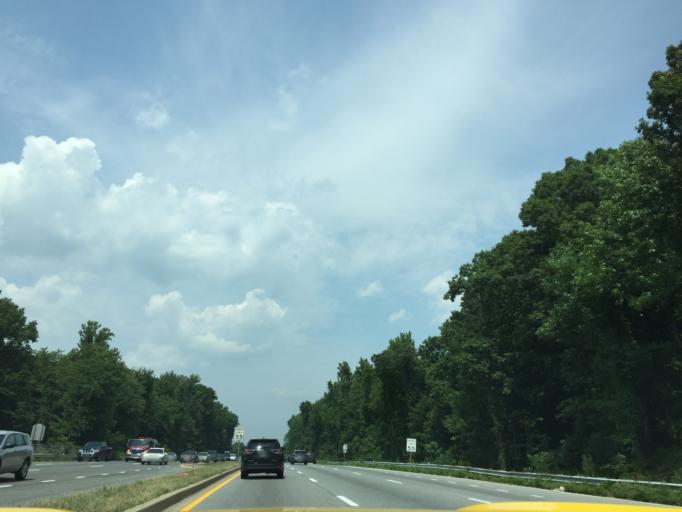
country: US
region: Maryland
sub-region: Prince George's County
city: Fort Washington
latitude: 38.7137
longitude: -76.9899
